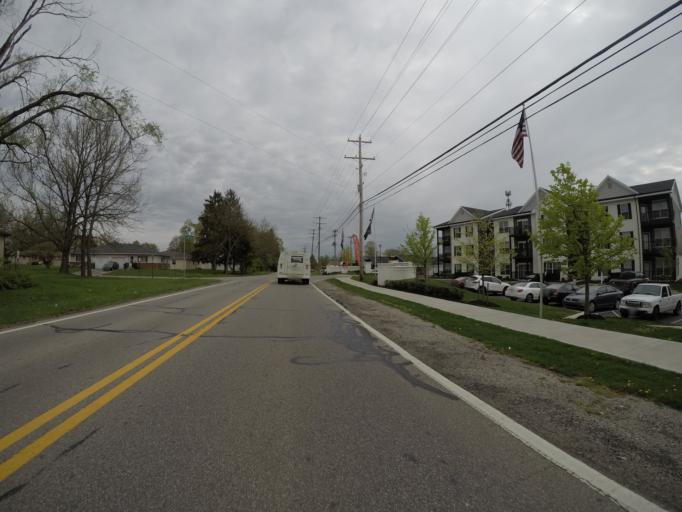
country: US
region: Ohio
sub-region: Franklin County
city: Worthington
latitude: 40.0602
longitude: -83.0483
